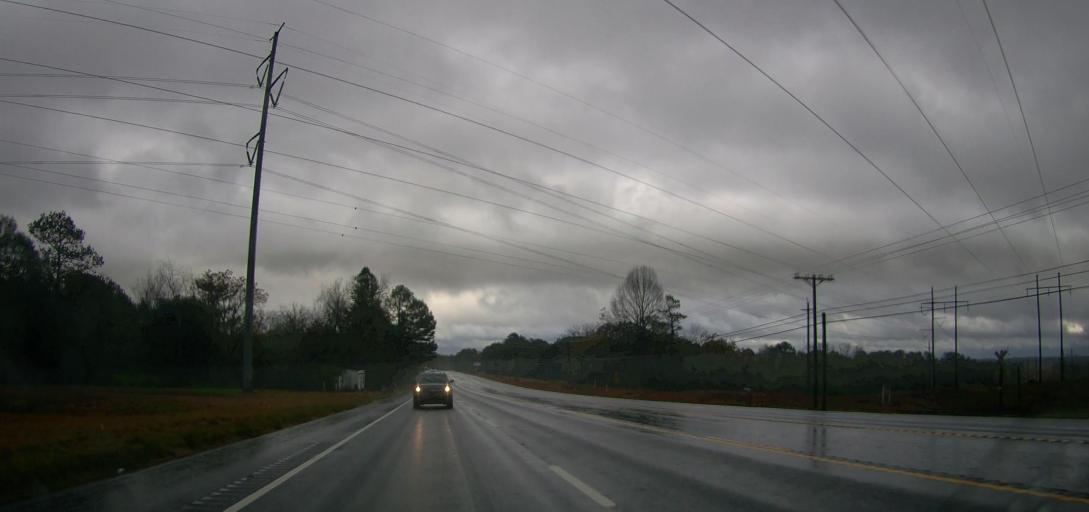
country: US
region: Georgia
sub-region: Clarke County
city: Country Club Estates
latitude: 34.0201
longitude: -83.3941
